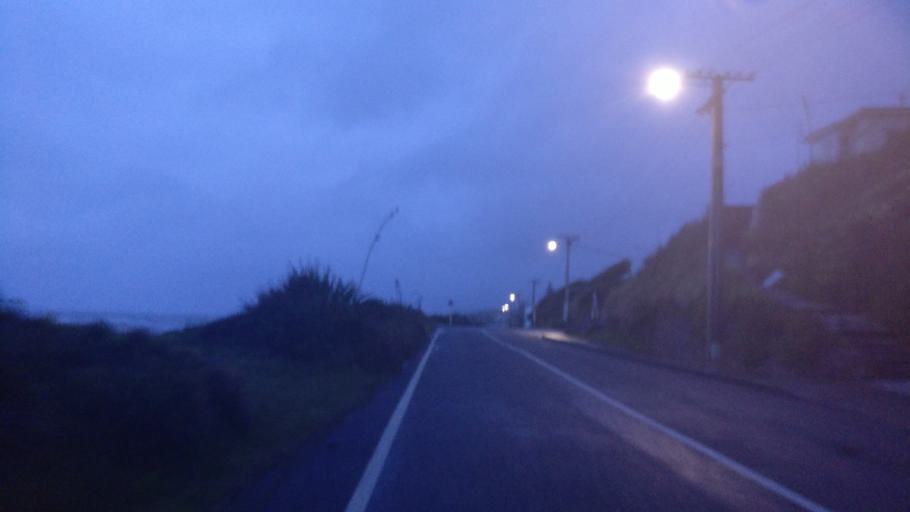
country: NZ
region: Wellington
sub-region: Kapiti Coast District
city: Paraparaumu
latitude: -40.9779
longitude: 174.9565
